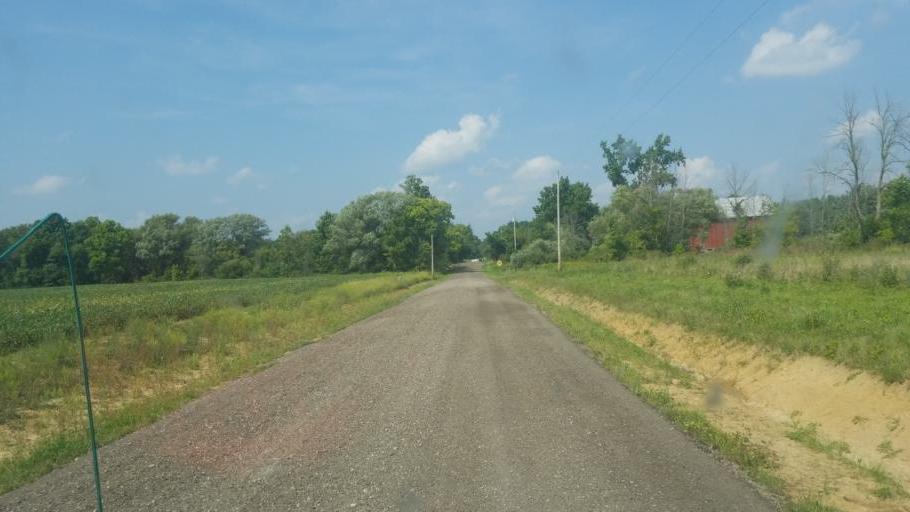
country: US
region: Ohio
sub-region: Huron County
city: New London
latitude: 41.0541
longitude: -82.4095
